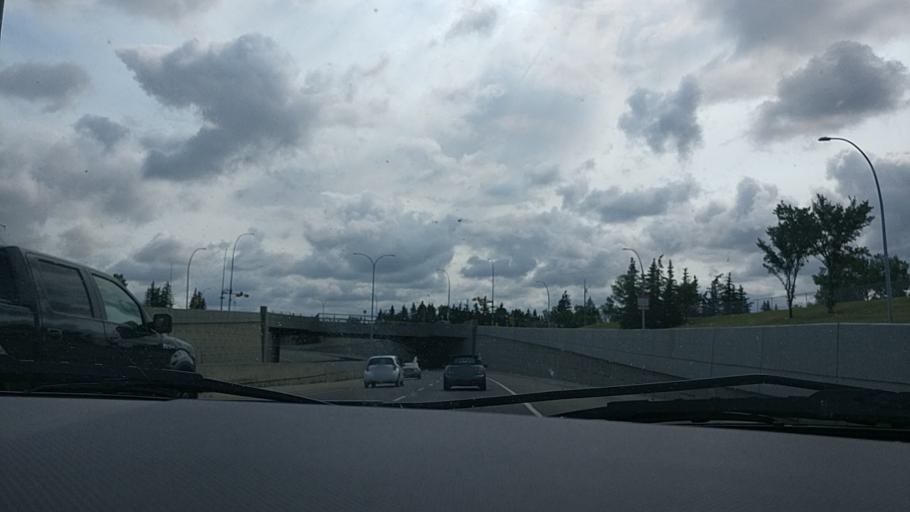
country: CA
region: Alberta
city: Calgary
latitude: 51.0900
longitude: -114.0969
